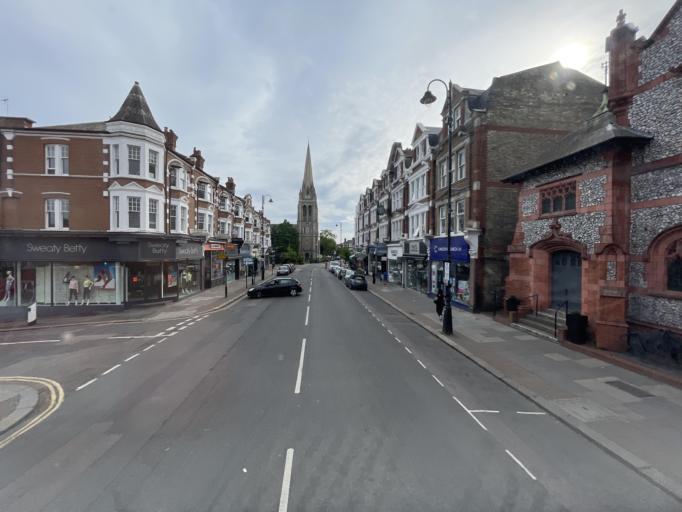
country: GB
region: England
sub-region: Greater London
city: Crouch End
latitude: 51.5901
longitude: -0.1440
